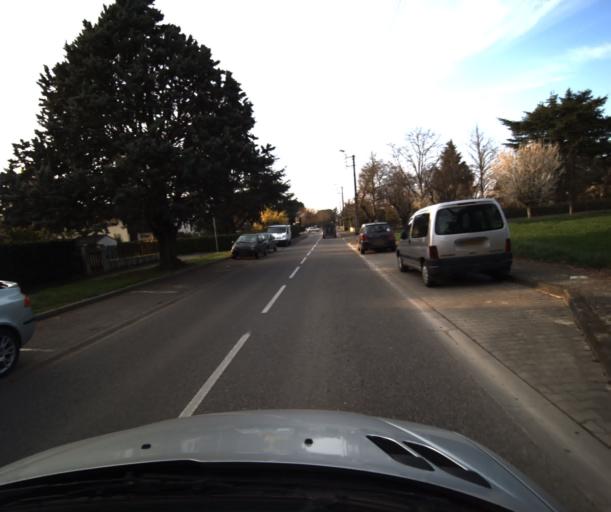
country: FR
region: Midi-Pyrenees
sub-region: Departement de la Haute-Garonne
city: Launaguet
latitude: 43.6777
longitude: 1.4553
